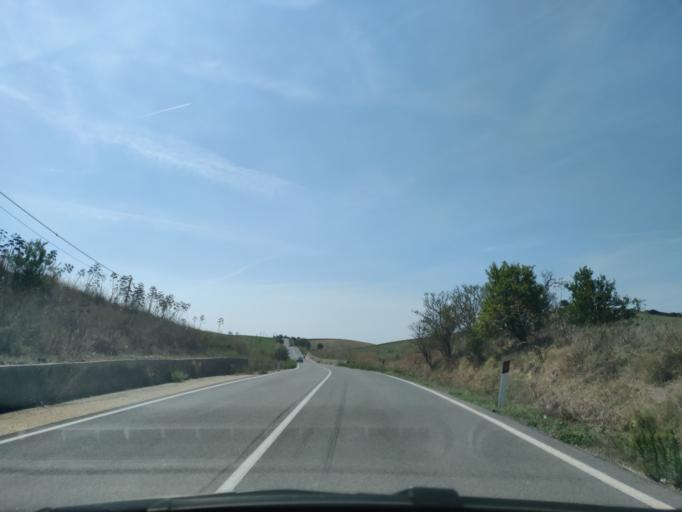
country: IT
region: Latium
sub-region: Provincia di Viterbo
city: Tarquinia
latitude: 42.2506
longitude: 11.8113
